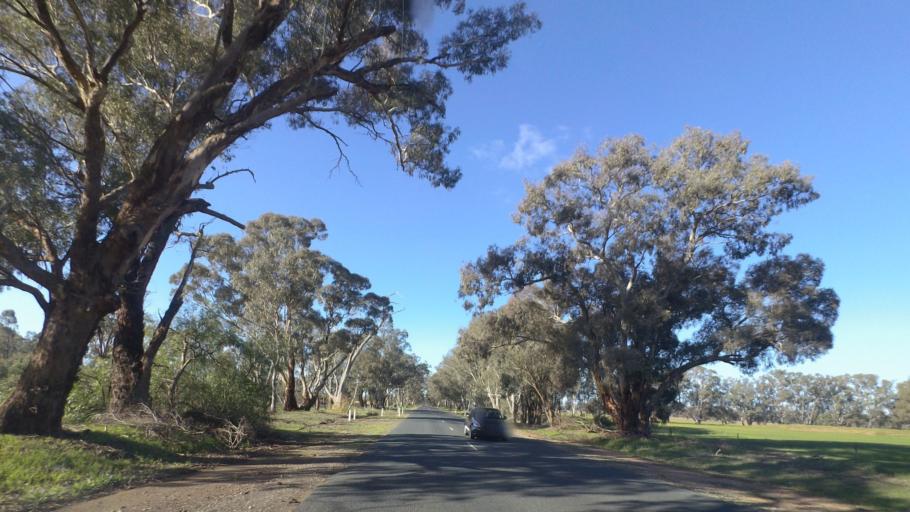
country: AU
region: Victoria
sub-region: Greater Bendigo
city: Epsom
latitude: -36.6613
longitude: 144.4596
